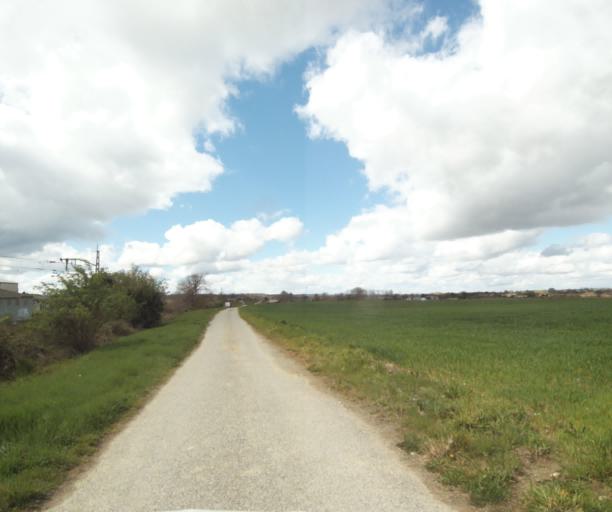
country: FR
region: Midi-Pyrenees
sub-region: Departement de l'Ariege
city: Saverdun
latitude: 43.2333
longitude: 1.5950
